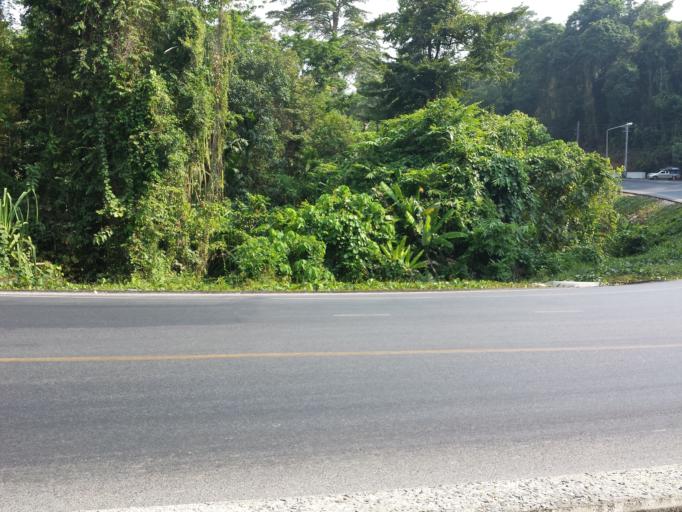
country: TH
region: Phangnga
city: Ban Khao Lak
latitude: 8.6229
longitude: 98.2366
